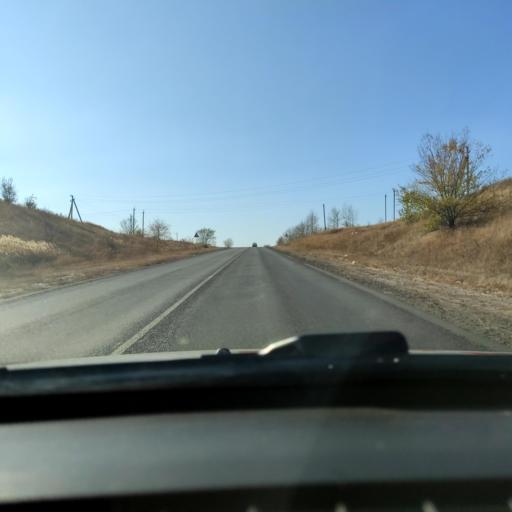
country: RU
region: Voronezj
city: Semiluki
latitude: 51.7259
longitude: 39.0131
